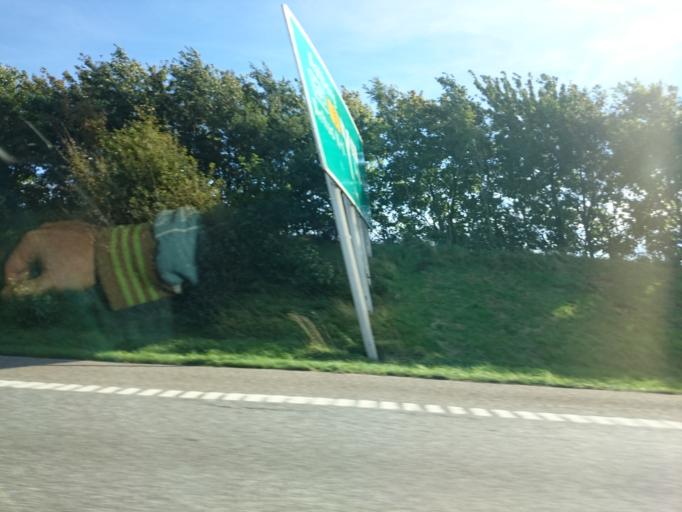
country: DK
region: Central Jutland
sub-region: Skanderborg Kommune
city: Stilling
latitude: 56.0772
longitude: 10.0042
